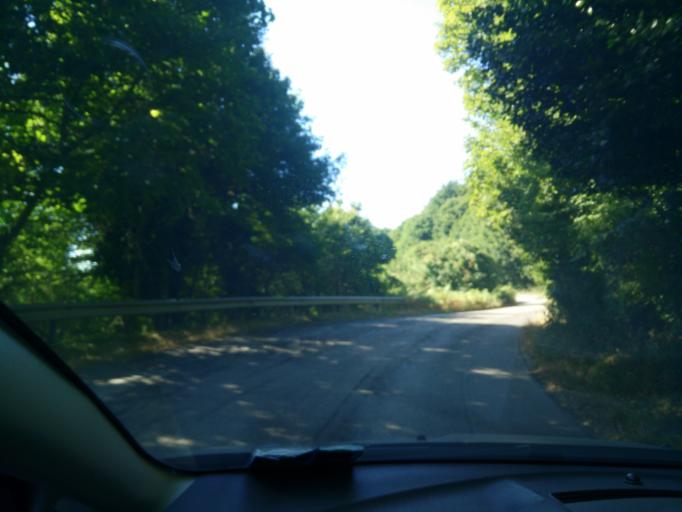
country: IT
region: Apulia
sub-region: Provincia di Foggia
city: Monte Sant'Angelo
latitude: 41.7928
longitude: 15.9792
